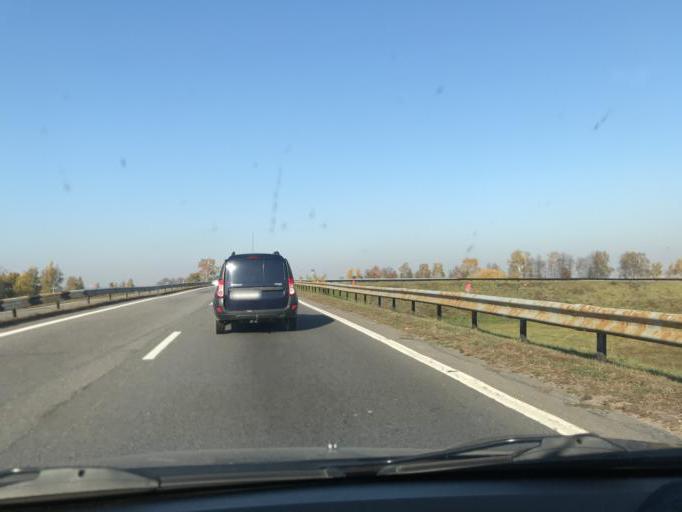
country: BY
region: Minsk
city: Luhavaya Slabada
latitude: 53.7885
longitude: 27.8205
